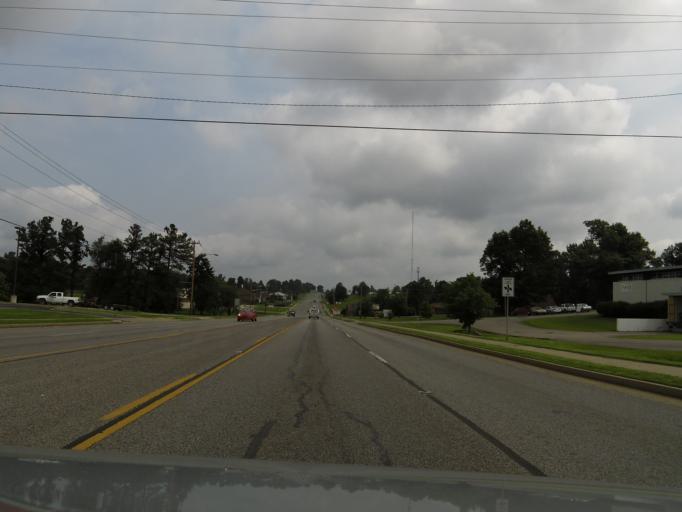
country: US
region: Kentucky
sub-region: Hopkins County
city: Madisonville
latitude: 37.3539
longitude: -87.4979
